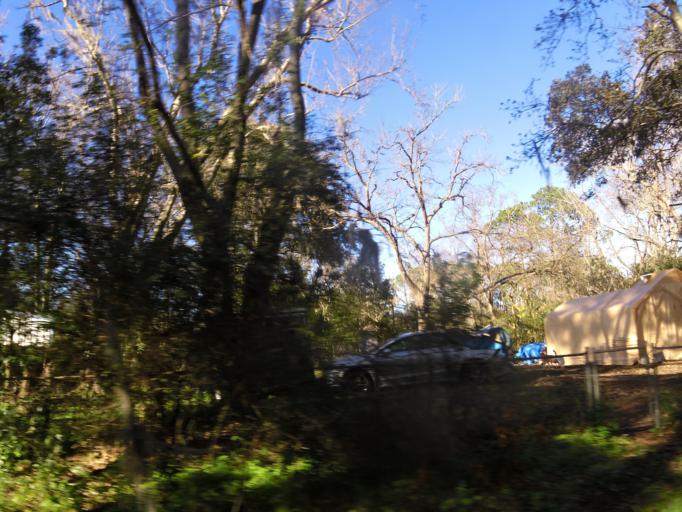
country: US
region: Florida
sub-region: Duval County
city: Jacksonville
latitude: 30.2724
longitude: -81.6293
